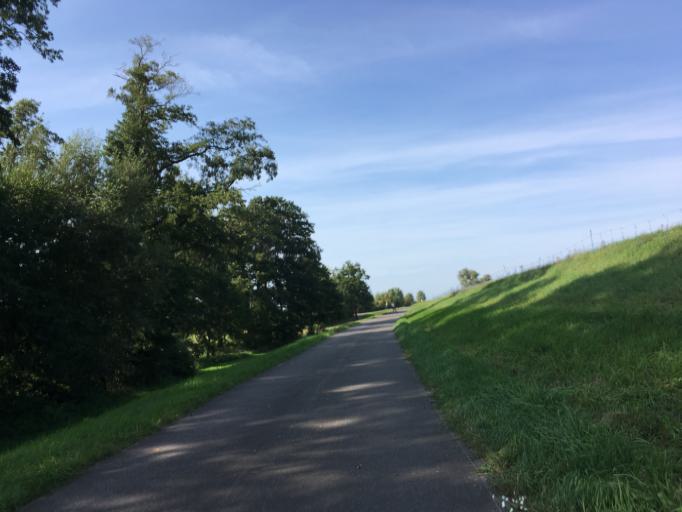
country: DE
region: Brandenburg
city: Vogelsang
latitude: 52.1838
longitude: 14.6878
